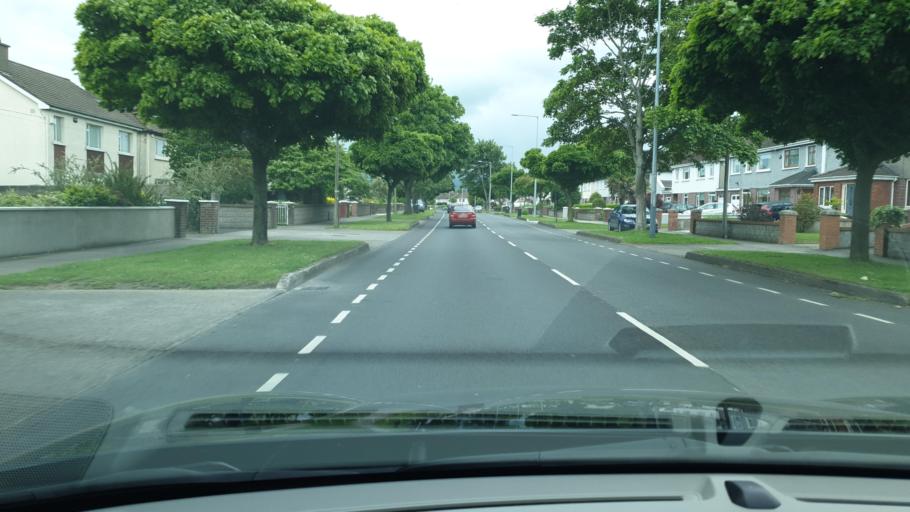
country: IE
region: Leinster
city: Crumlin
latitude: 53.3097
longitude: -6.3252
